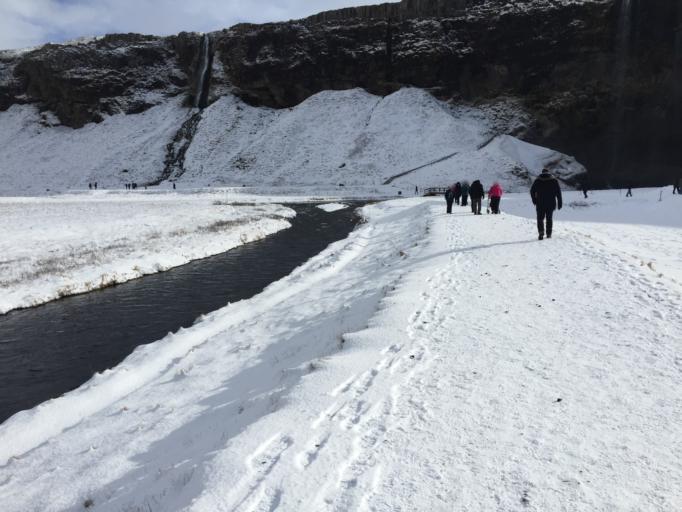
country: IS
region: South
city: Vestmannaeyjar
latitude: 63.6160
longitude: -19.9917
